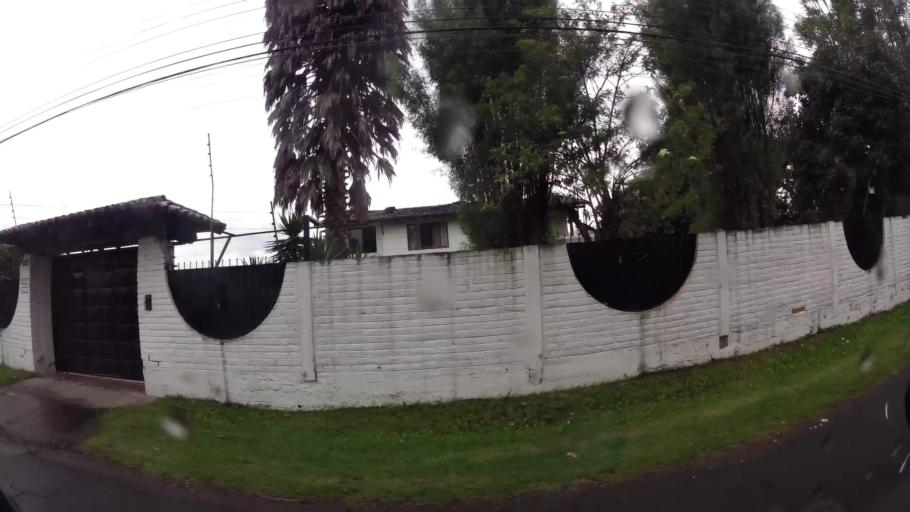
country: EC
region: Pichincha
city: Sangolqui
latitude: -0.2844
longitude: -78.4528
